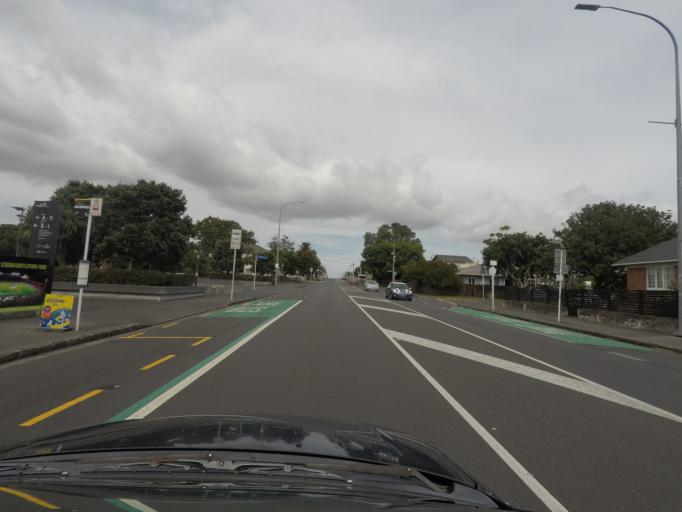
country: NZ
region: Auckland
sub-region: Auckland
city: Auckland
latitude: -36.8751
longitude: 174.7417
